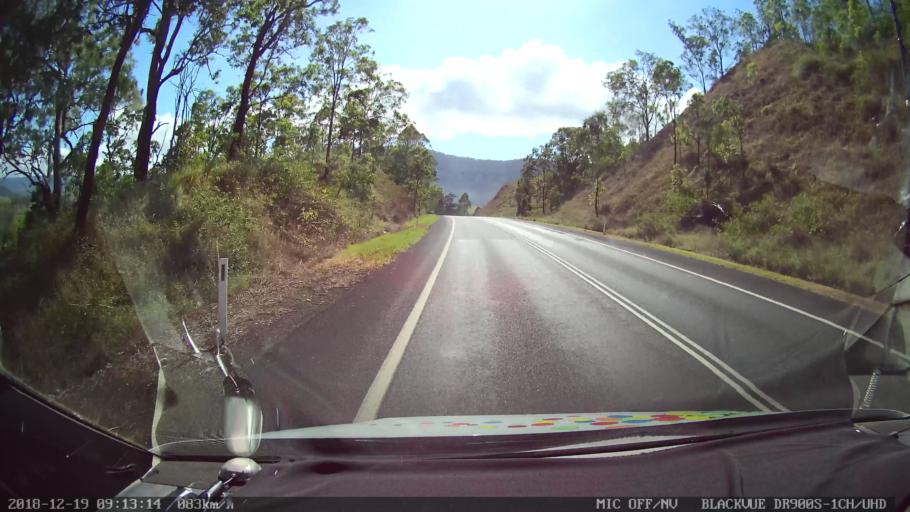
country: AU
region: New South Wales
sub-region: Kyogle
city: Kyogle
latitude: -28.5020
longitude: 152.9600
